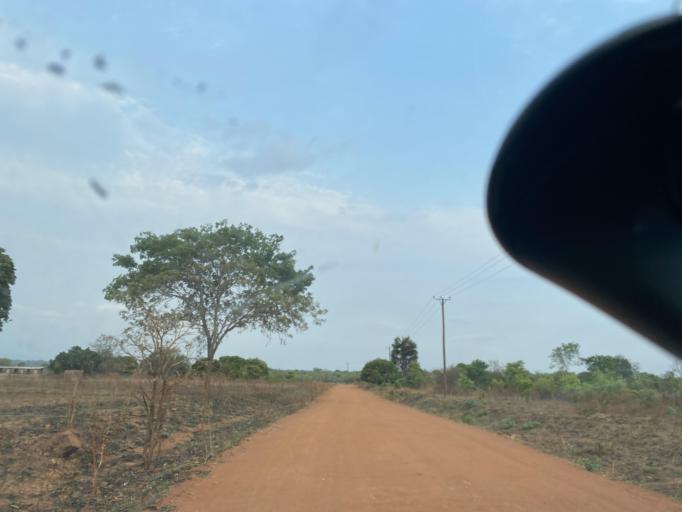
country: ZM
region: Lusaka
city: Chongwe
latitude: -15.2411
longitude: 28.6024
